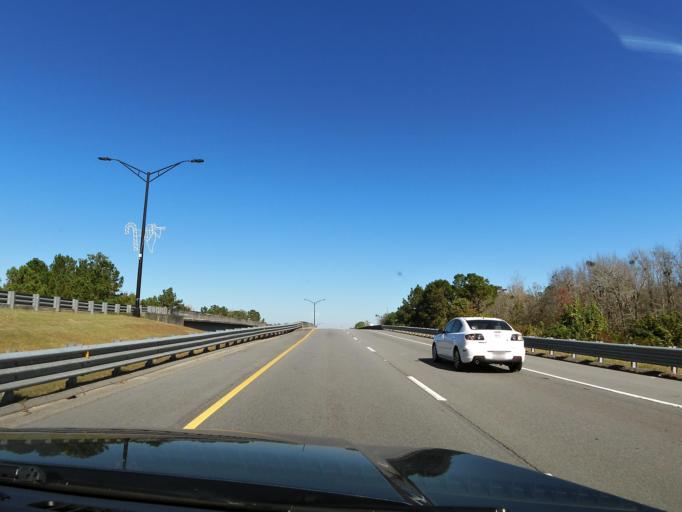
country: US
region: Georgia
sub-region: Bryan County
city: Richmond Hill
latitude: 31.9363
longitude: -81.3203
